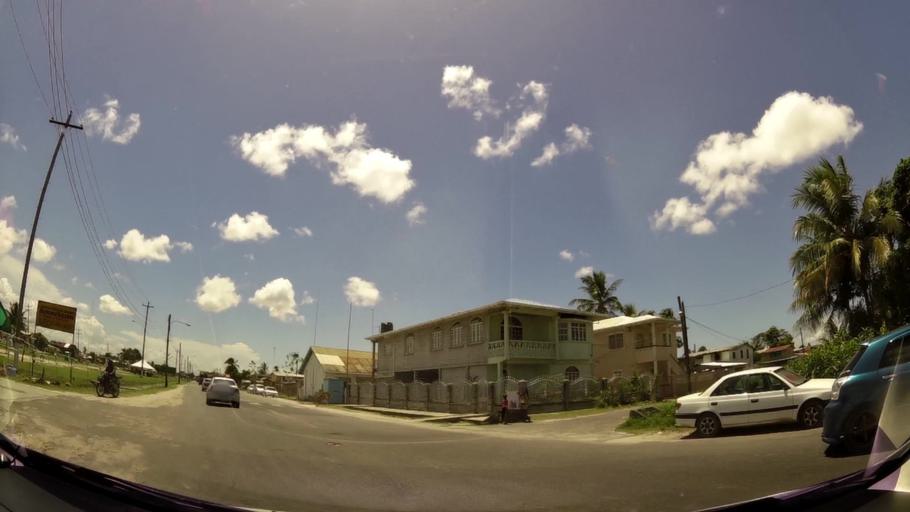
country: GY
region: Demerara-Mahaica
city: Georgetown
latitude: 6.7894
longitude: -58.1506
